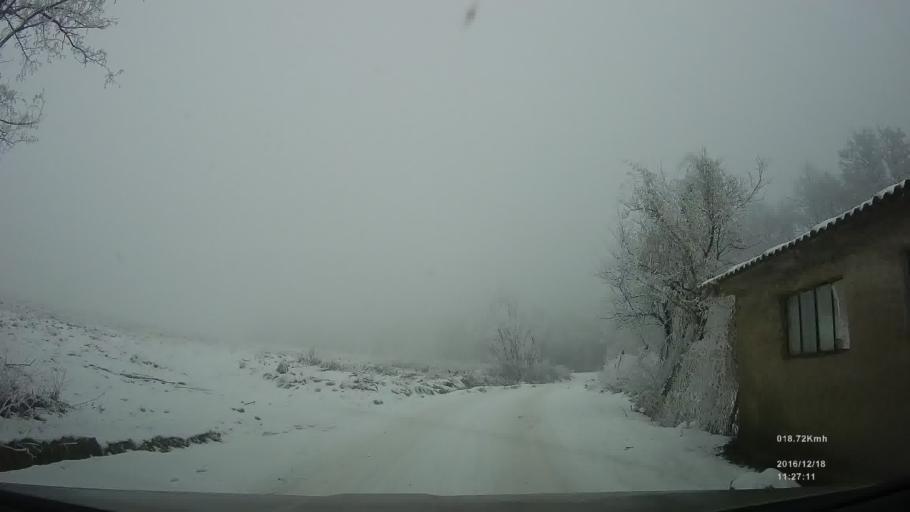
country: SK
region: Presovsky
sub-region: Okres Presov
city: Presov
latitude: 48.9018
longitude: 21.4078
